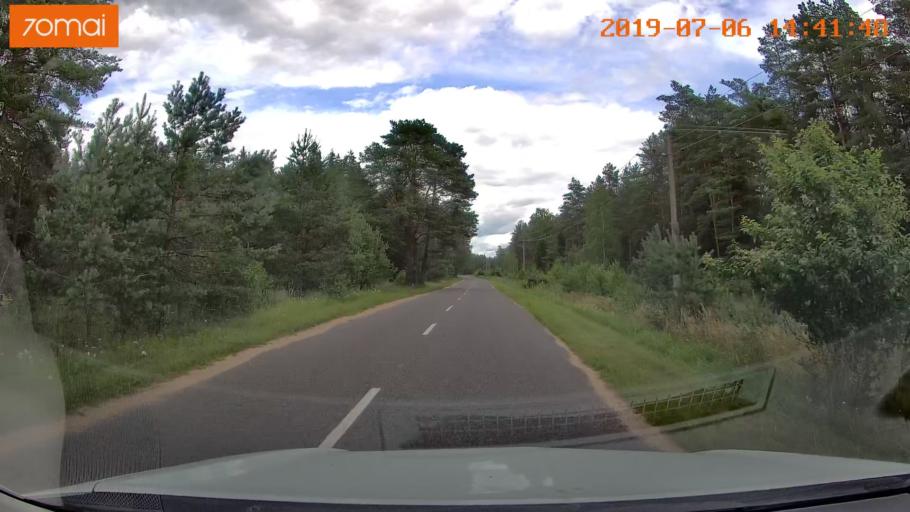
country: BY
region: Minsk
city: Ivyanyets
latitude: 53.9357
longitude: 26.6818
